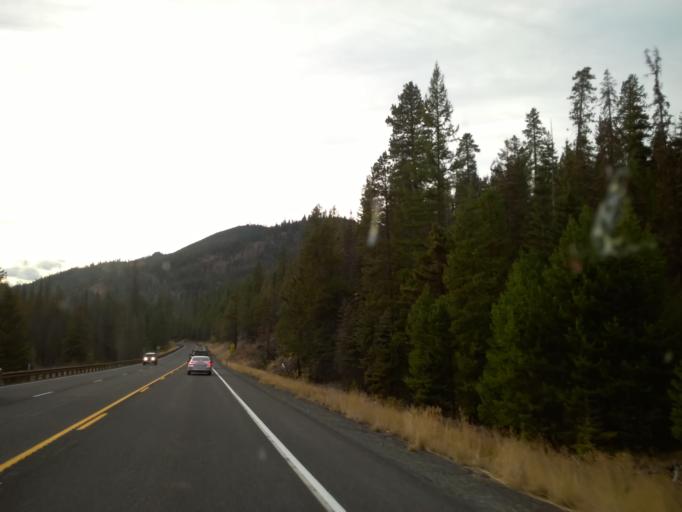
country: US
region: Washington
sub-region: Chelan County
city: Cashmere
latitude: 47.3329
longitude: -120.6169
